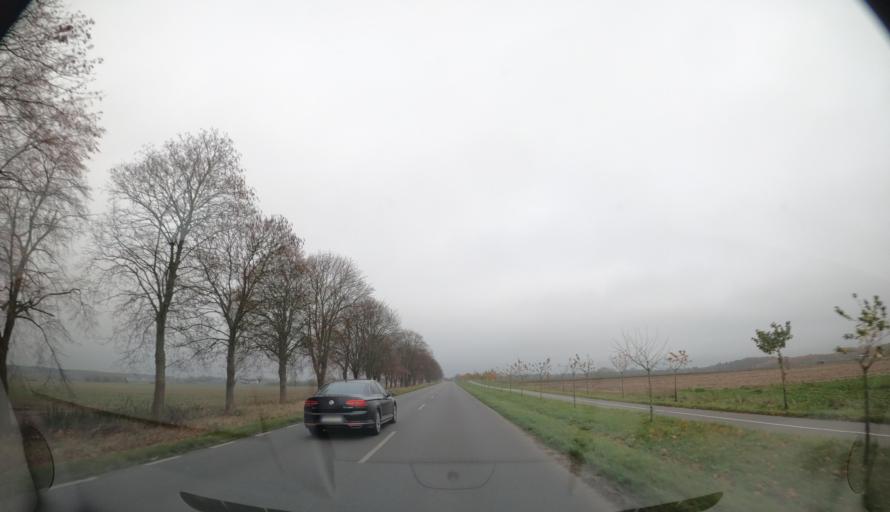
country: PL
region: West Pomeranian Voivodeship
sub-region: Powiat goleniowski
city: Goleniow
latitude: 53.5834
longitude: 14.8597
